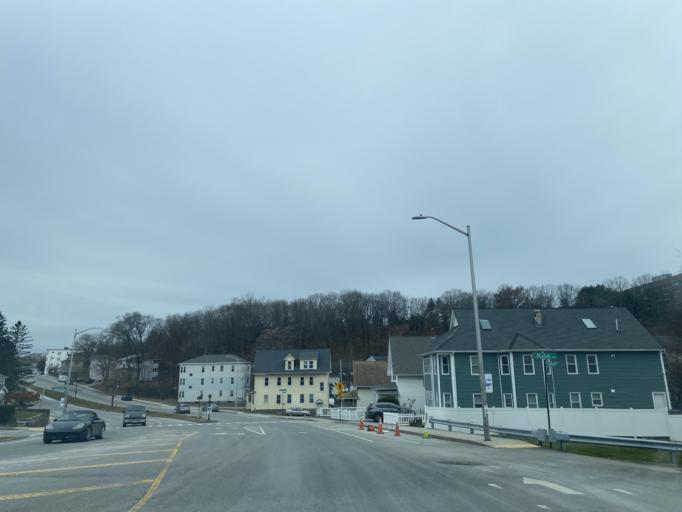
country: US
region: Massachusetts
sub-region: Worcester County
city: Hamilton
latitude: 42.2596
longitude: -71.7640
